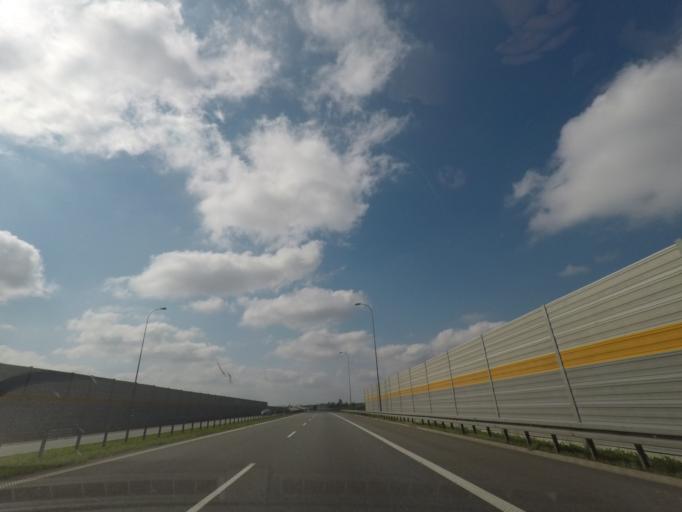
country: PL
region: Kujawsko-Pomorskie
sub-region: Powiat torunski
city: Lubicz Dolny
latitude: 53.1382
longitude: 18.7406
